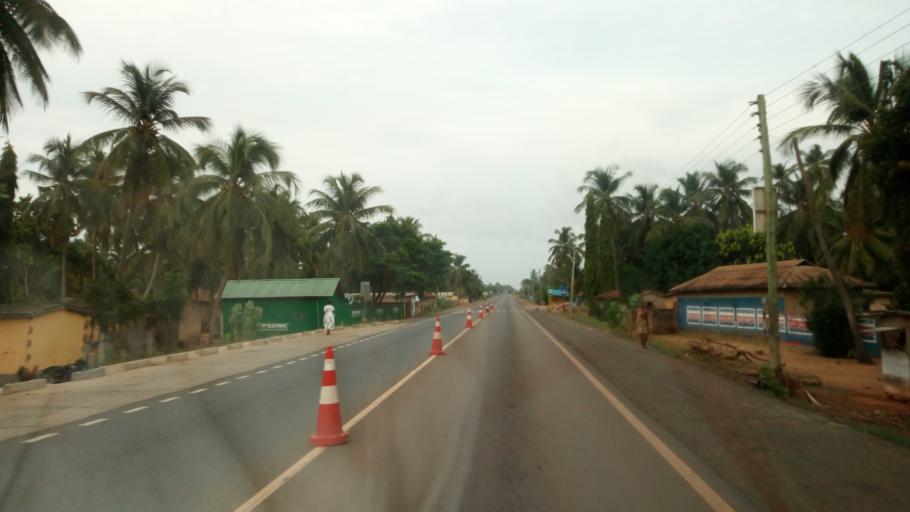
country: TG
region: Maritime
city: Lome
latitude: 6.0877
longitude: 1.0641
